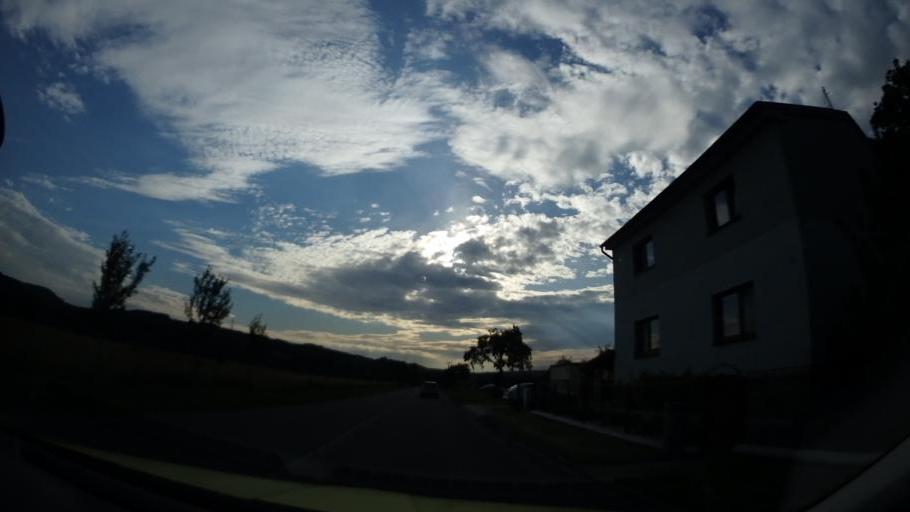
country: CZ
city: Stramberk
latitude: 49.5934
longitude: 18.1088
